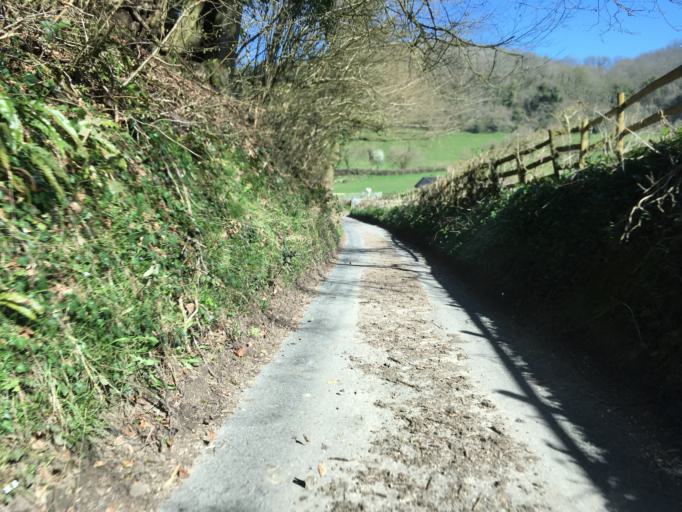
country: GB
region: England
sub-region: Gloucestershire
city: Wotton-under-Edge
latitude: 51.6507
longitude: -2.3454
